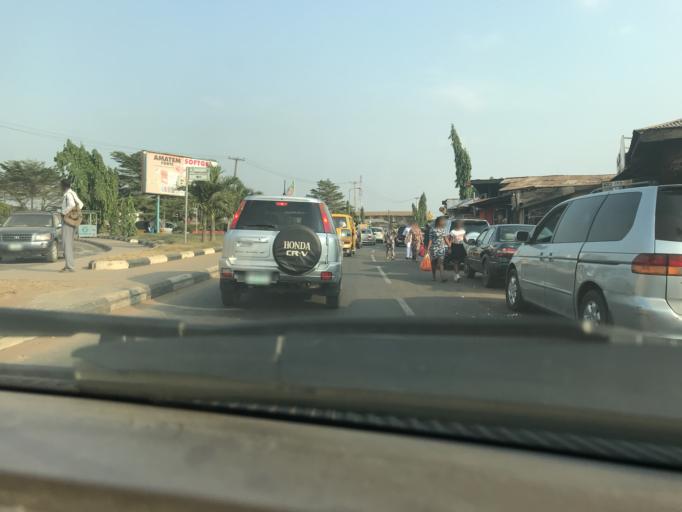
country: NG
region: Lagos
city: Ikotun
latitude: 6.5765
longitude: 3.2803
